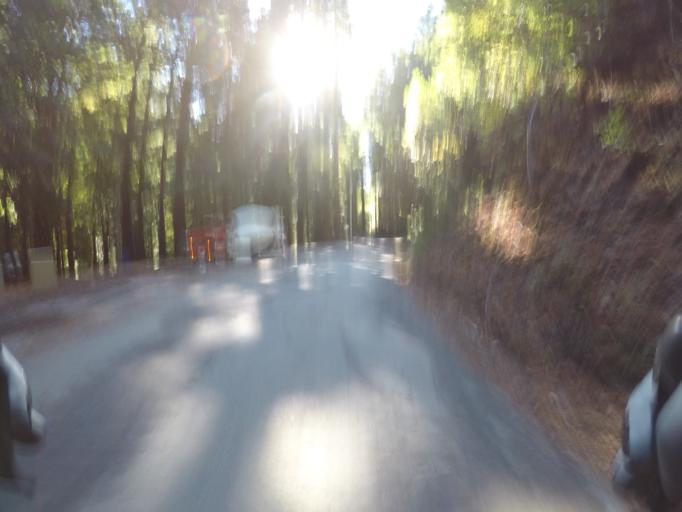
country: US
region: California
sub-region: Santa Cruz County
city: Lompico
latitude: 37.1424
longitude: -122.0214
